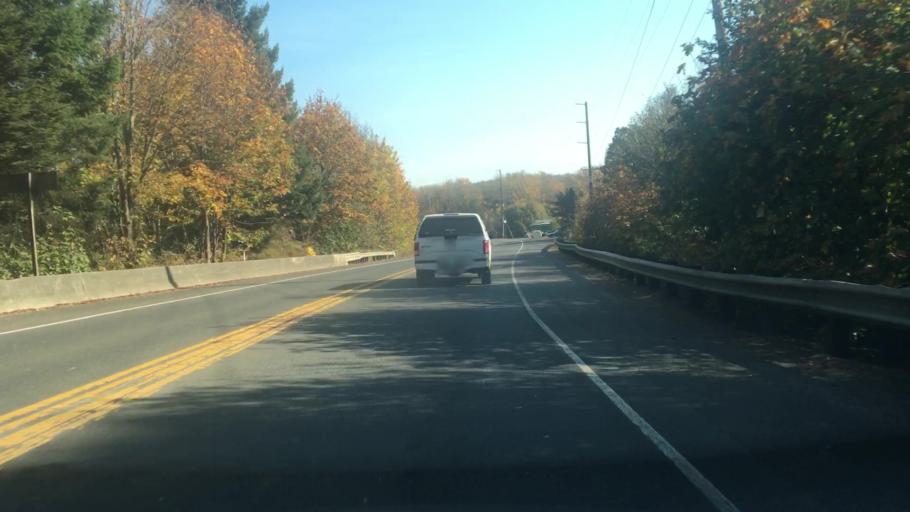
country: US
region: Oregon
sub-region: Polk County
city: Grand Ronde
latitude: 45.0591
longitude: -123.6067
